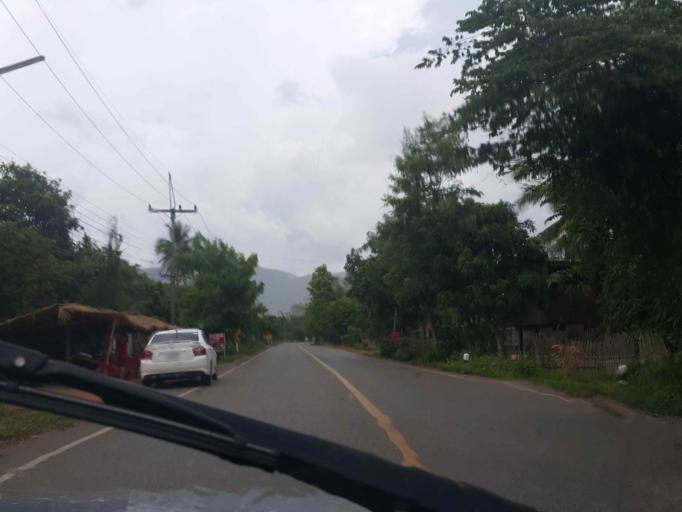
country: TH
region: Phayao
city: Dok Kham Tai
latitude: 19.0503
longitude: 100.0526
